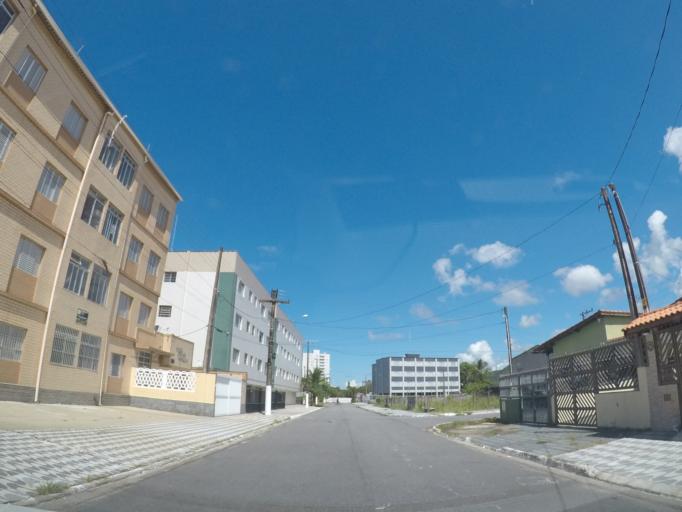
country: BR
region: Sao Paulo
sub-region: Mongagua
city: Mongagua
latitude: -24.0821
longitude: -46.5937
